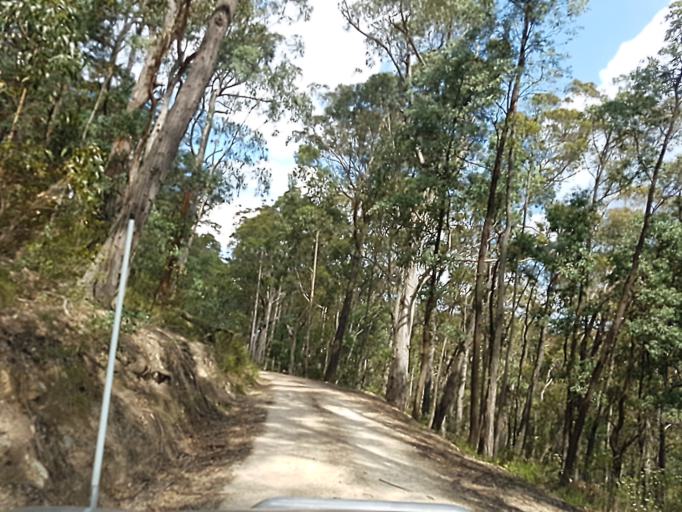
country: AU
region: Victoria
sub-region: East Gippsland
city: Lakes Entrance
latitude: -37.4108
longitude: 148.2347
